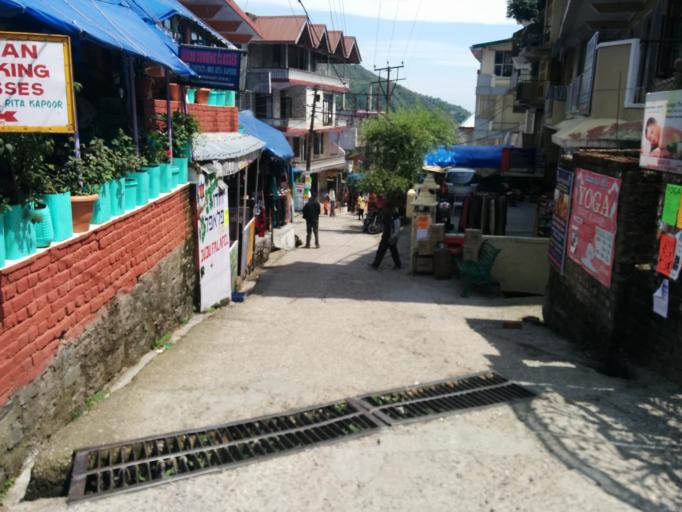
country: IN
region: Himachal Pradesh
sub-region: Kangra
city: Dharmsala
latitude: 32.2452
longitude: 76.3325
